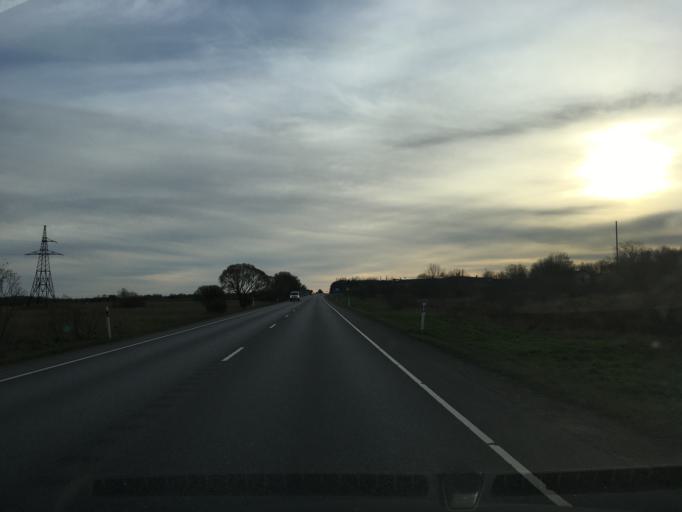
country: EE
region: Ida-Virumaa
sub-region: Kohtla-Jaerve linn
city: Kohtla-Jarve
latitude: 59.4128
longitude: 27.3034
